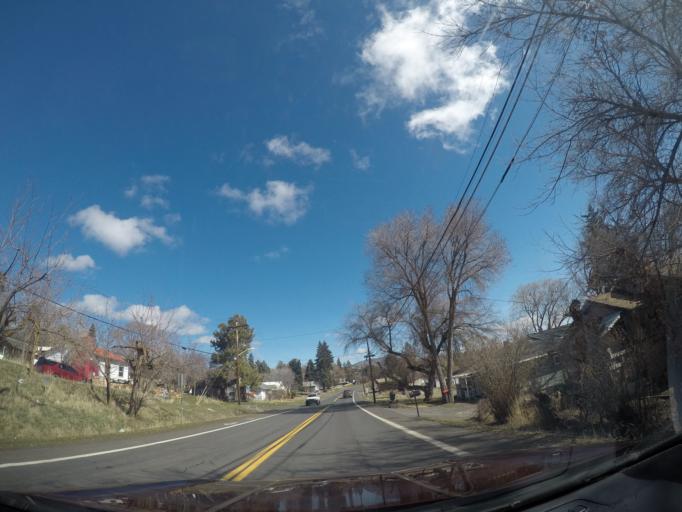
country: US
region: Oregon
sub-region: Klamath County
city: Klamath Falls
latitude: 42.2395
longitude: -121.8022
